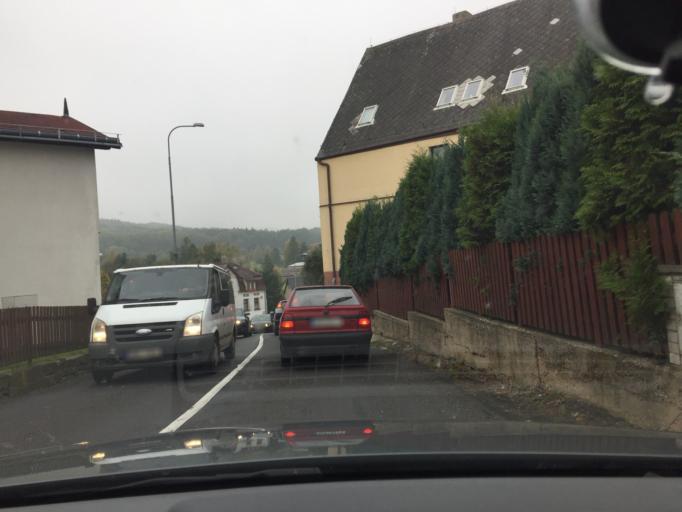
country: CZ
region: Ustecky
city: Libouchec
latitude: 50.7614
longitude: 14.0450
